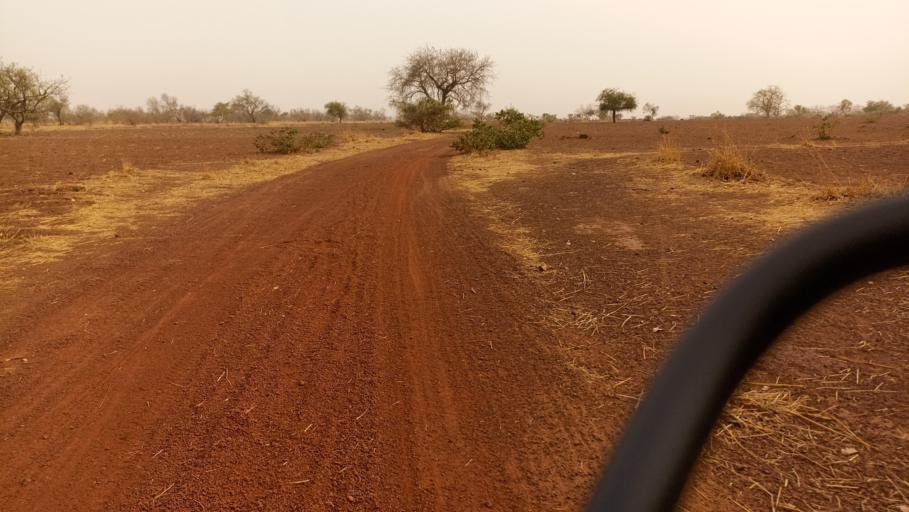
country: BF
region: Nord
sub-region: Province du Zondoma
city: Gourcy
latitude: 13.1491
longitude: -2.5965
